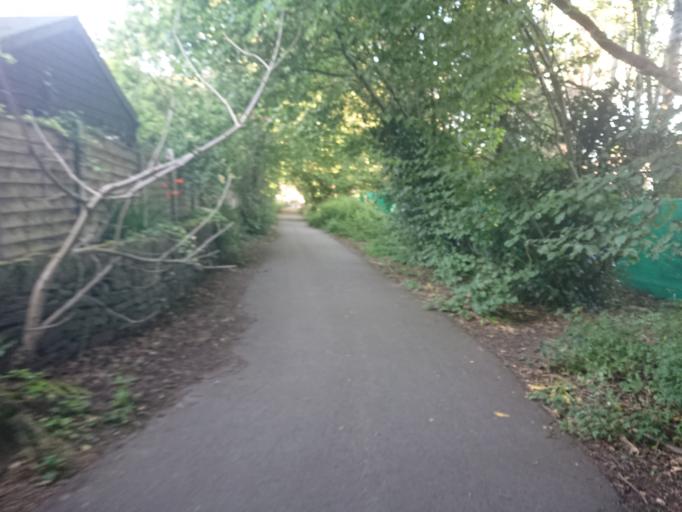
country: GB
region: England
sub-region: Sheffield
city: Sheffield
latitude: 53.3483
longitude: -1.5090
